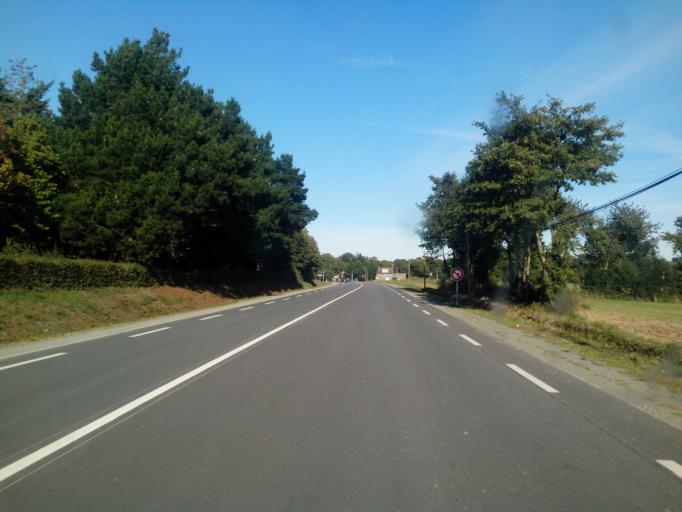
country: FR
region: Brittany
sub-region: Departement du Morbihan
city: Mauron
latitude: 48.0286
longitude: -2.3104
